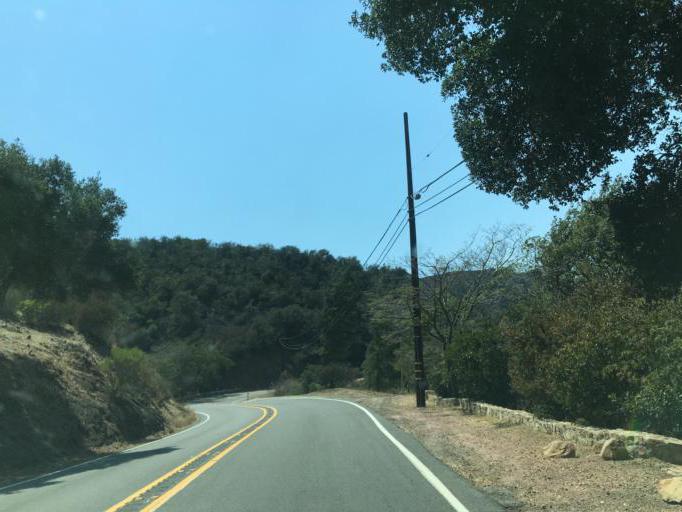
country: US
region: California
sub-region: Los Angeles County
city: Malibu Beach
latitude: 34.0723
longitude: -118.6875
